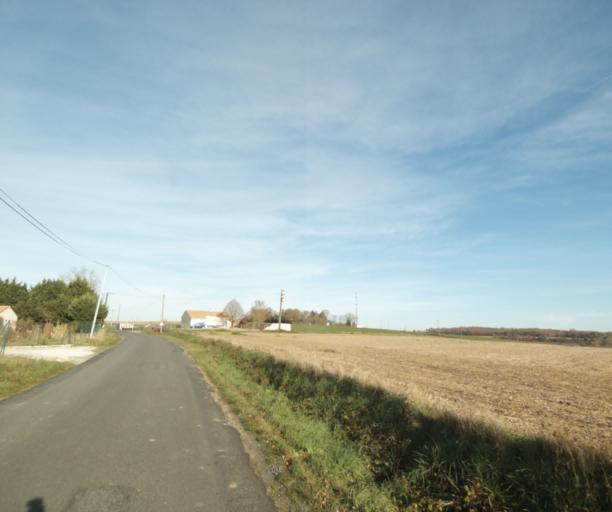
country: FR
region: Poitou-Charentes
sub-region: Departement de la Charente-Maritime
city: Chaniers
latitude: 45.7130
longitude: -0.5315
